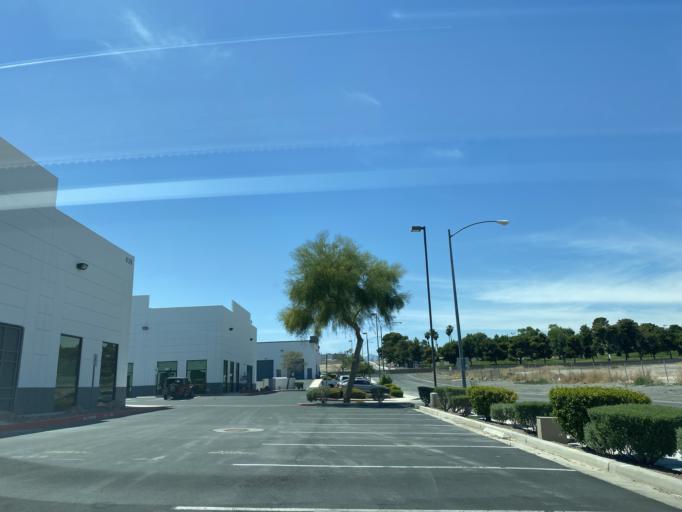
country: US
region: Nevada
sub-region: Clark County
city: North Las Vegas
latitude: 36.2139
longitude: -115.1320
